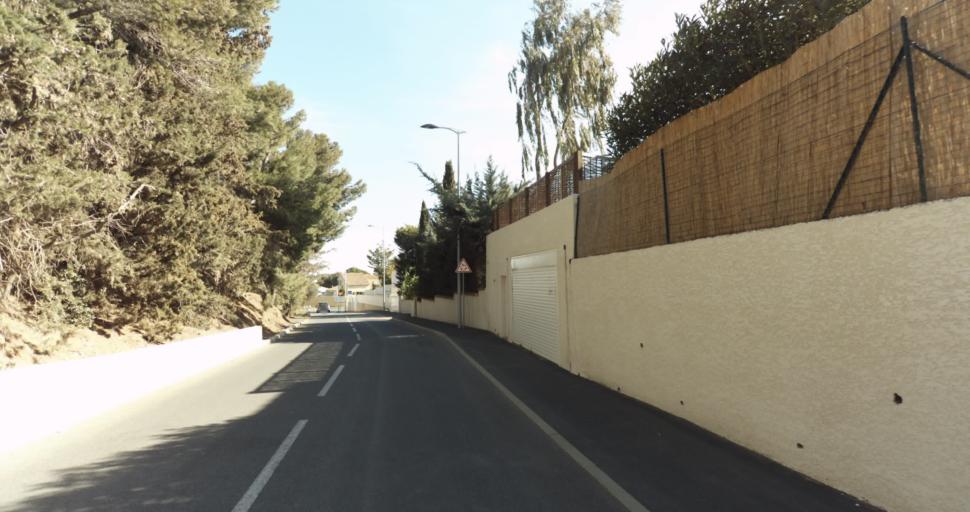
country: FR
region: Languedoc-Roussillon
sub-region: Departement de l'Herault
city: Marseillan
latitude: 43.3530
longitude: 3.5235
